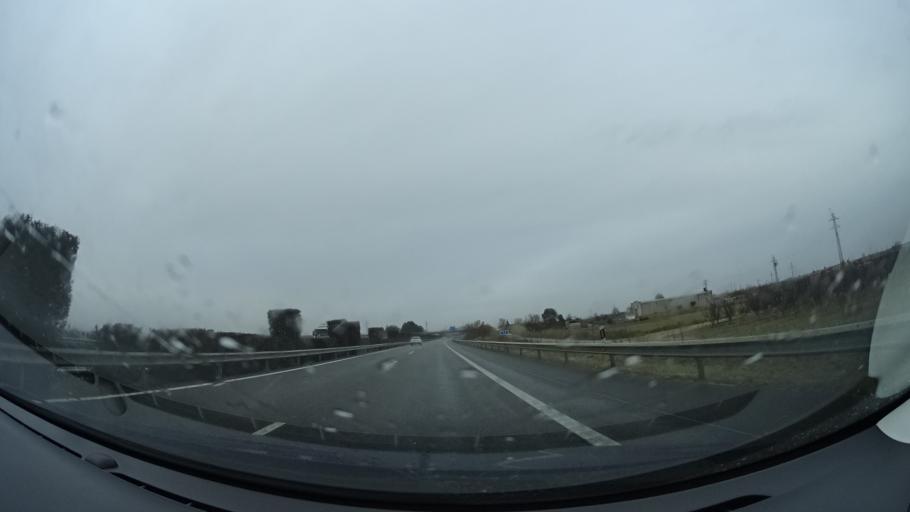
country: ES
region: Catalonia
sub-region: Provincia de Lleida
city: Lleida
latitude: 41.5695
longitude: 0.6224
